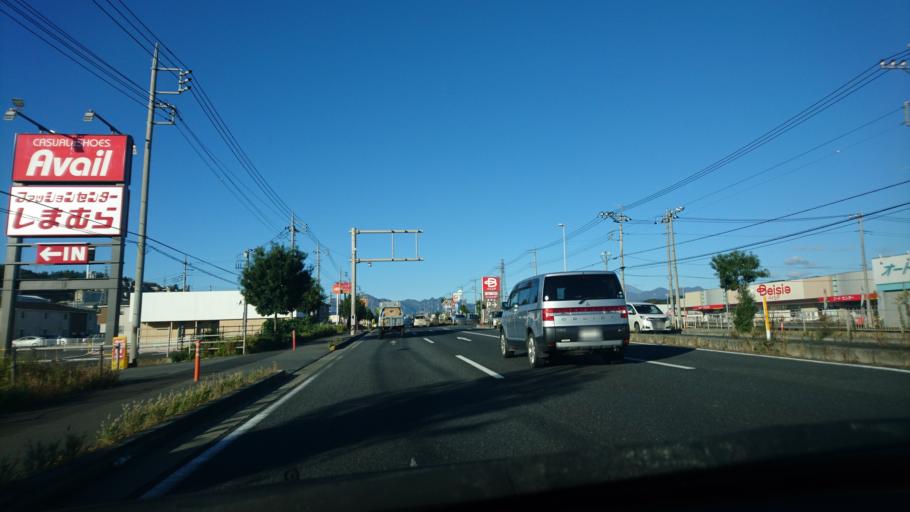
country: JP
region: Gunma
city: Annaka
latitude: 36.3330
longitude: 138.9261
